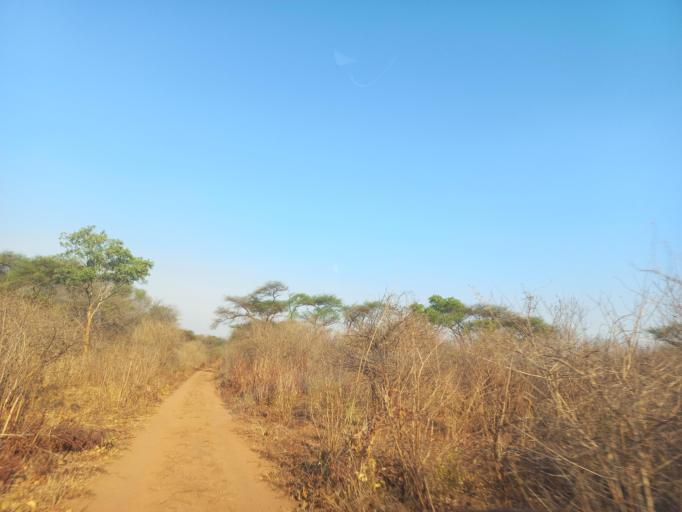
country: ZM
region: Lusaka
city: Luangwa
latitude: -15.4175
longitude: 30.2497
